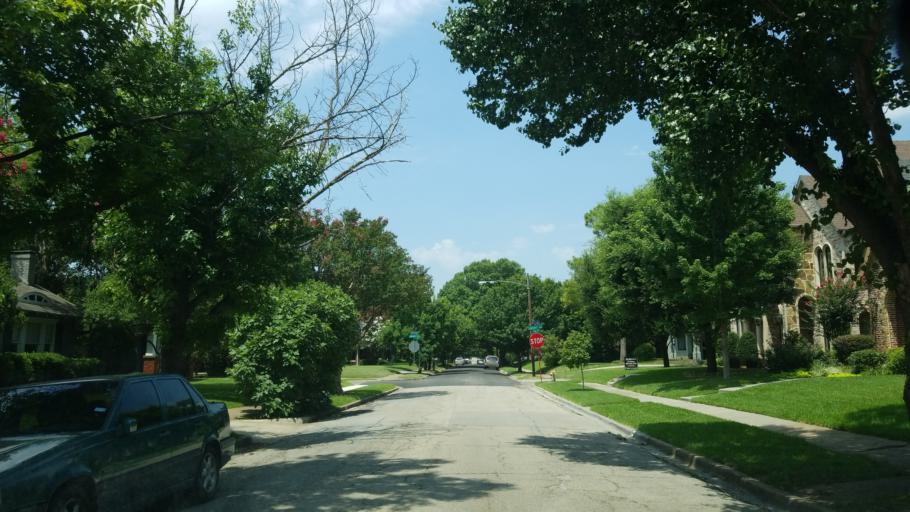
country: US
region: Texas
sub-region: Dallas County
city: Highland Park
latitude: 32.8235
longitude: -96.7794
